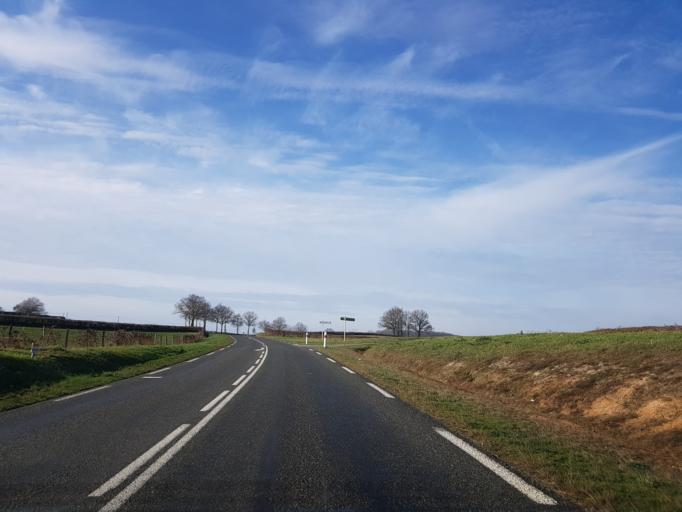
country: FR
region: Bourgogne
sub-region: Departement de Saone-et-Loire
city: Bourbon-Lancy
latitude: 46.6054
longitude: 3.8914
